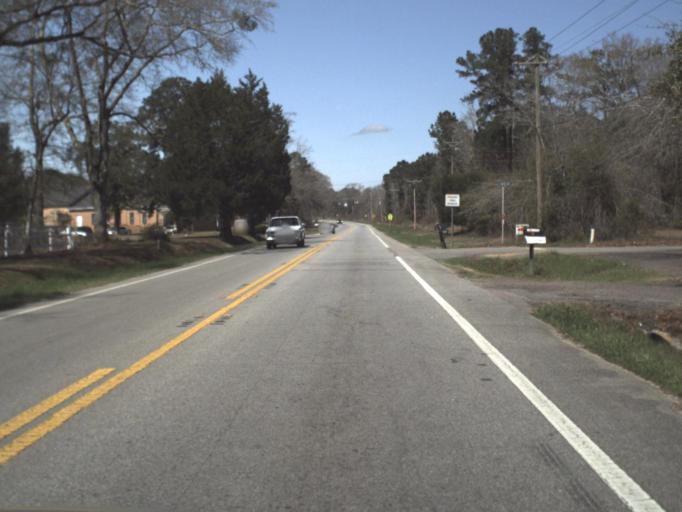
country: US
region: Florida
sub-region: Gadsden County
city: Gretna
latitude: 30.6573
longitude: -84.6049
